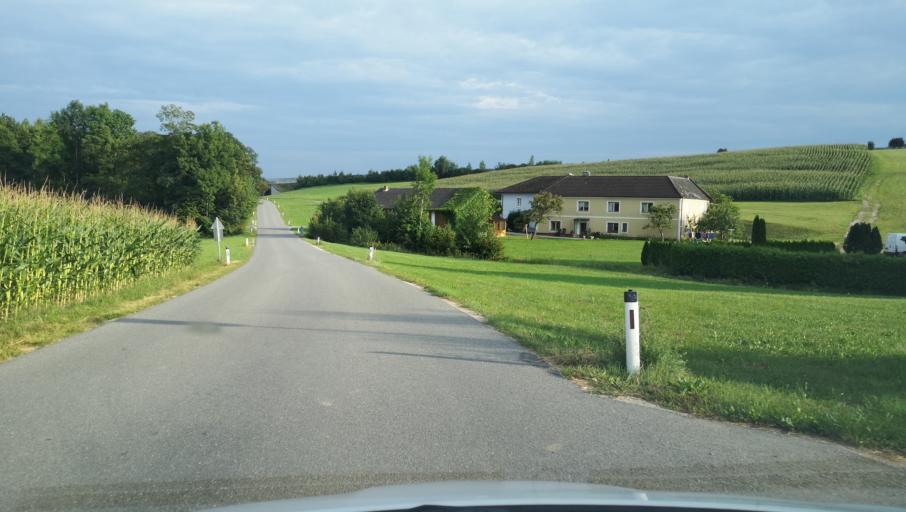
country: AT
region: Lower Austria
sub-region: Politischer Bezirk Melk
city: Blindenmarkt
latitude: 48.1399
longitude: 14.9740
